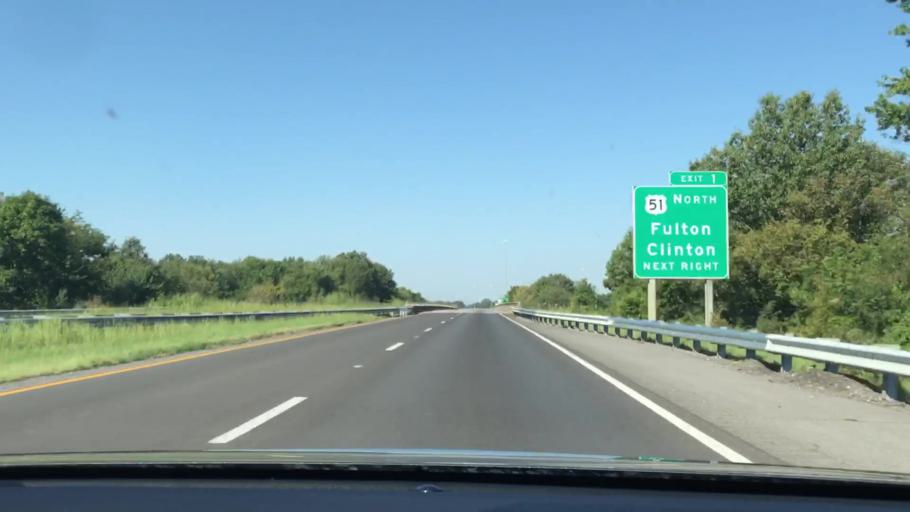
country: US
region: Kentucky
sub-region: Fulton County
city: Fulton
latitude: 36.5184
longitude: -88.8812
